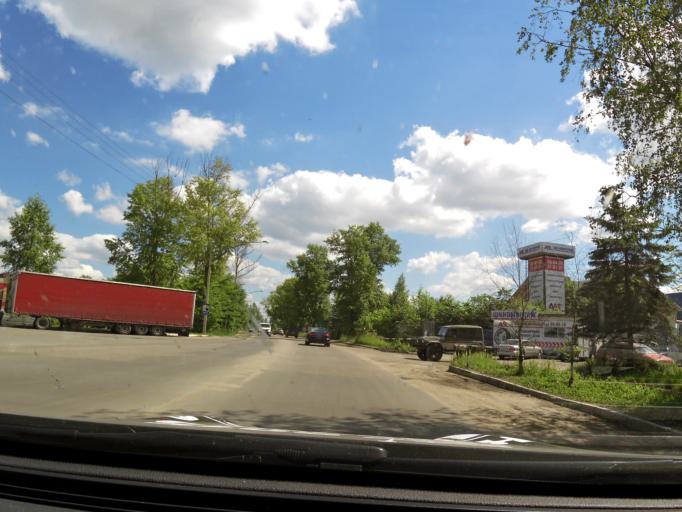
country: RU
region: Vologda
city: Vologda
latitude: 59.2348
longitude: 39.8289
